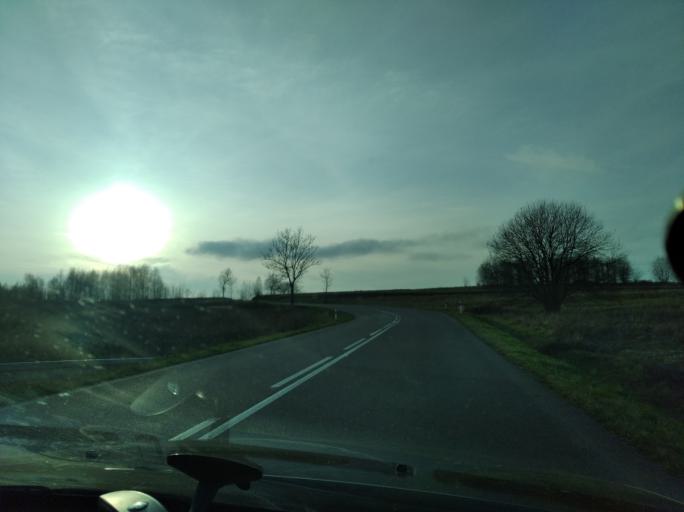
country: PL
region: Subcarpathian Voivodeship
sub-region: Powiat brzozowski
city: Wesola
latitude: 49.8259
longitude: 22.0753
